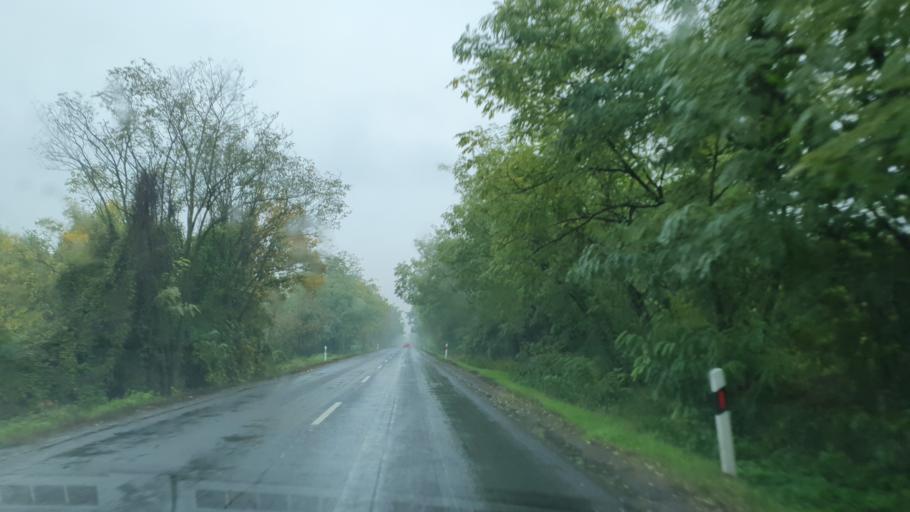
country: HU
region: Pest
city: Nagymaros
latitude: 47.8134
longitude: 18.9753
